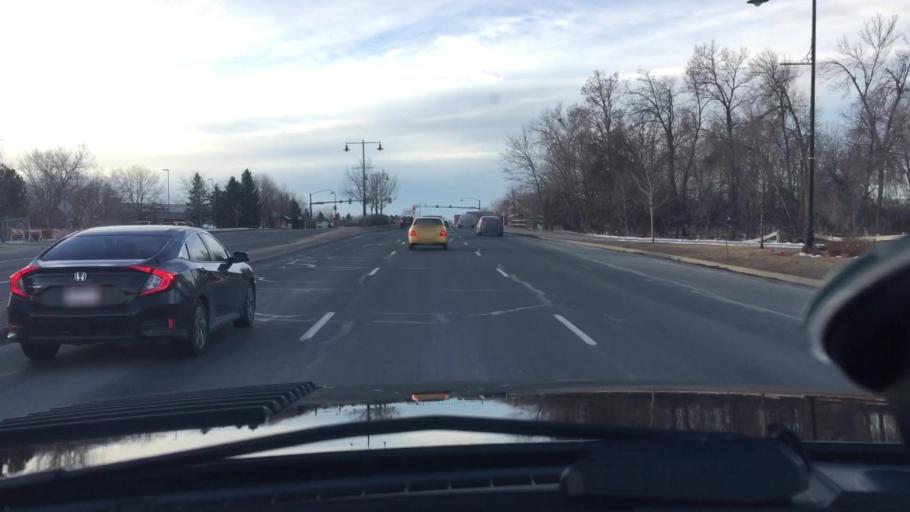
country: US
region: Colorado
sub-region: Adams County
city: Westminster
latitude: 39.8700
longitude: -105.0533
